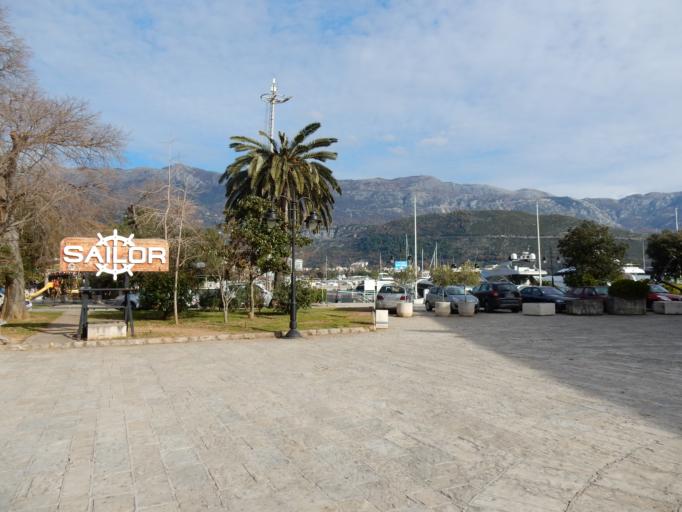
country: ME
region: Budva
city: Budva
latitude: 42.2790
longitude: 18.8373
